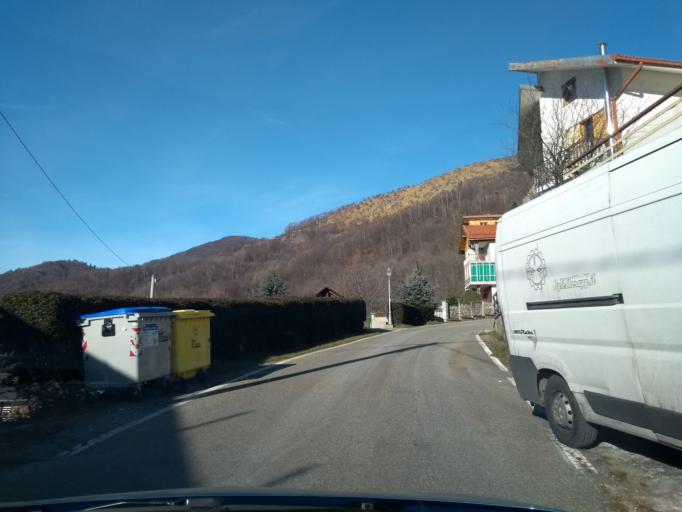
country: IT
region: Piedmont
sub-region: Provincia di Torino
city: Pessinetto
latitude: 45.2844
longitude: 7.4315
